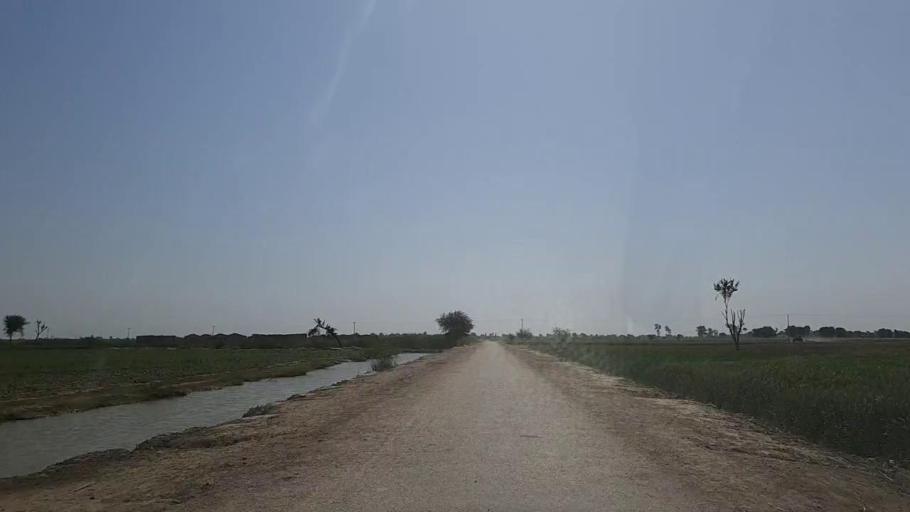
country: PK
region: Sindh
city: Samaro
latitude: 25.2313
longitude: 69.4557
